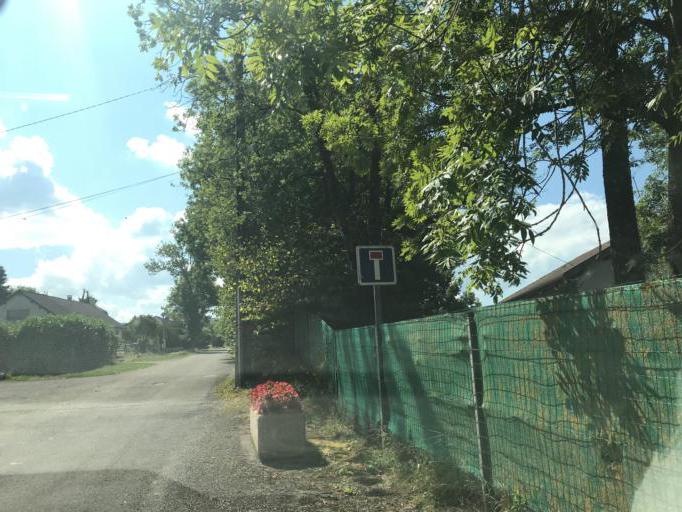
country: FR
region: Franche-Comte
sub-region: Departement du Jura
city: Moirans-en-Montagne
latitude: 46.4644
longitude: 5.7089
